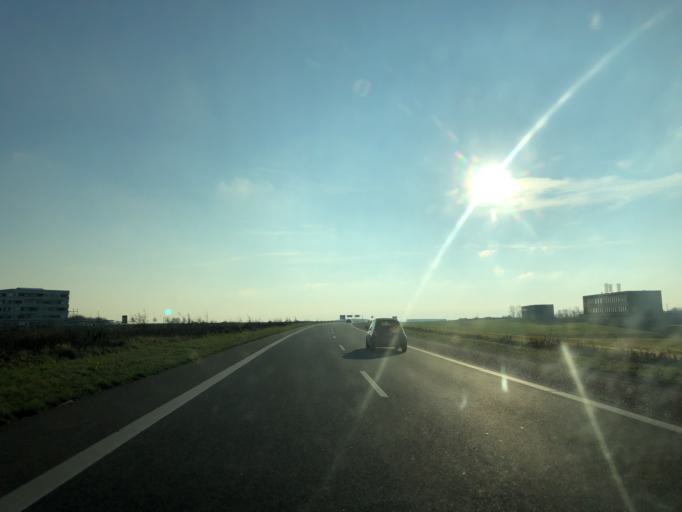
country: DK
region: South Denmark
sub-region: Vejle Kommune
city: Vejle
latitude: 55.7459
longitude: 9.5800
